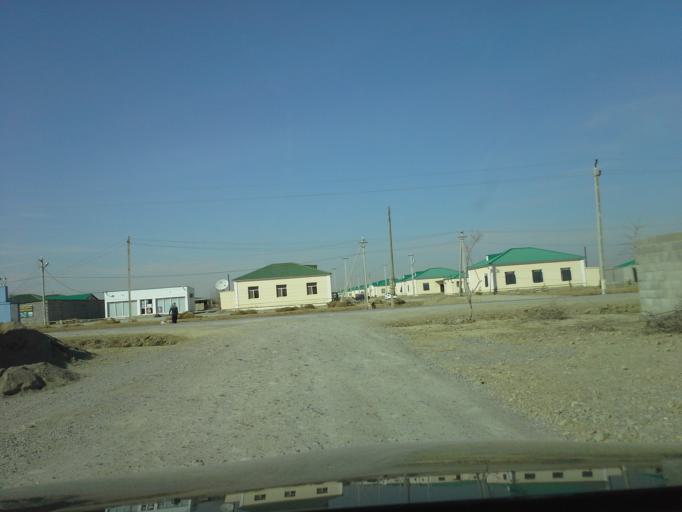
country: TM
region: Ahal
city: Abadan
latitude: 38.1306
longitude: 58.0034
